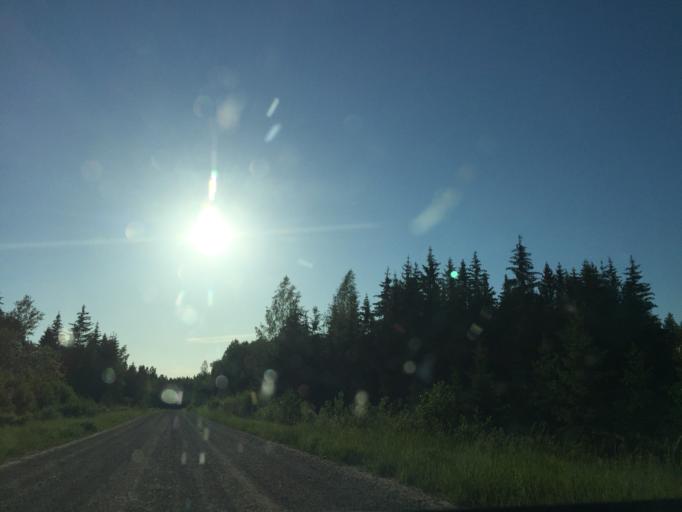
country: LV
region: Talsu Rajons
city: Sabile
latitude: 56.8649
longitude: 22.6483
